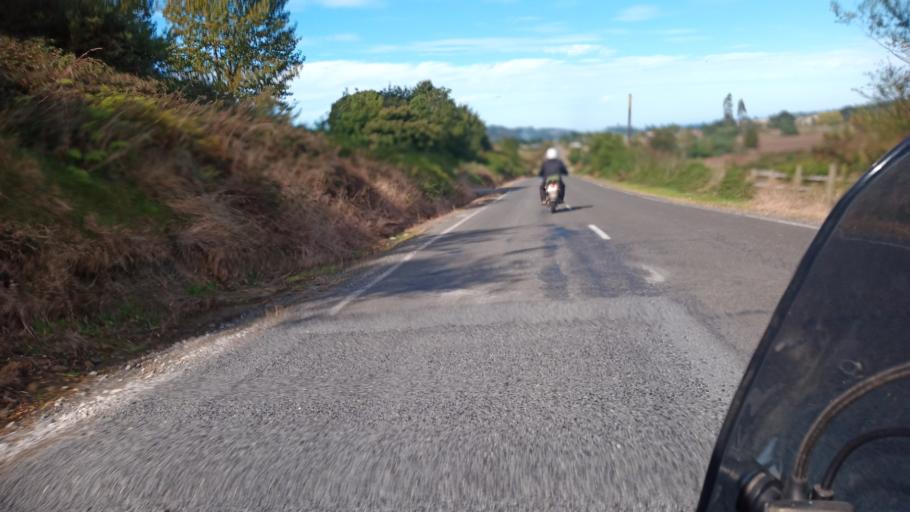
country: NZ
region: Hawke's Bay
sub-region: Wairoa District
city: Wairoa
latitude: -39.0661
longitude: 177.1358
